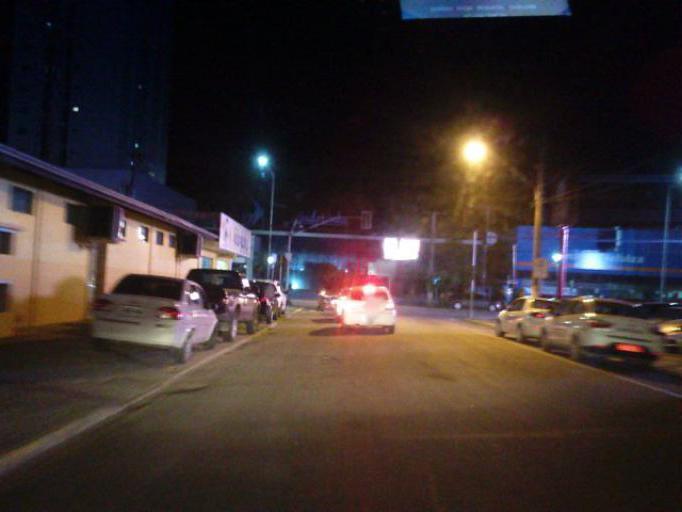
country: BR
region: Santa Catarina
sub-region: Itapema
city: Itapema
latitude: -27.1191
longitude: -48.6086
